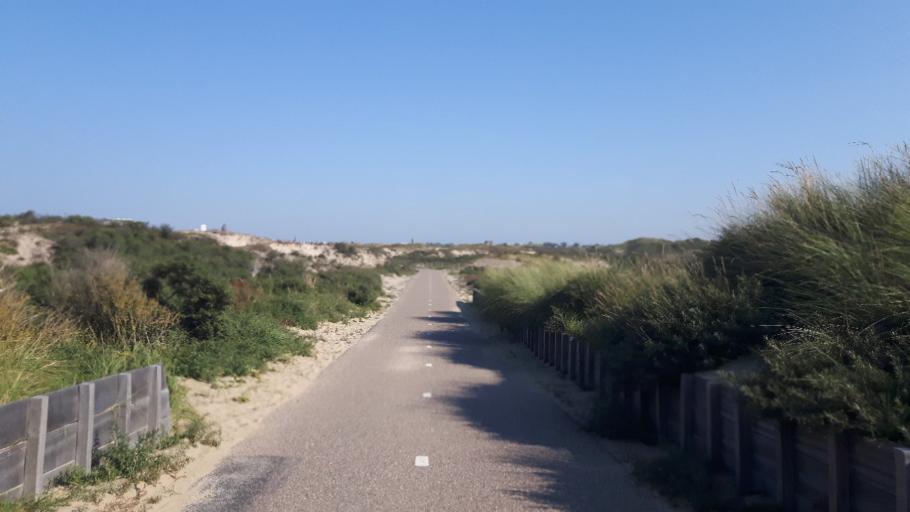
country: NL
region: North Holland
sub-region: Gemeente Zandvoort
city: Zandvoort
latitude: 52.3546
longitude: 4.5153
